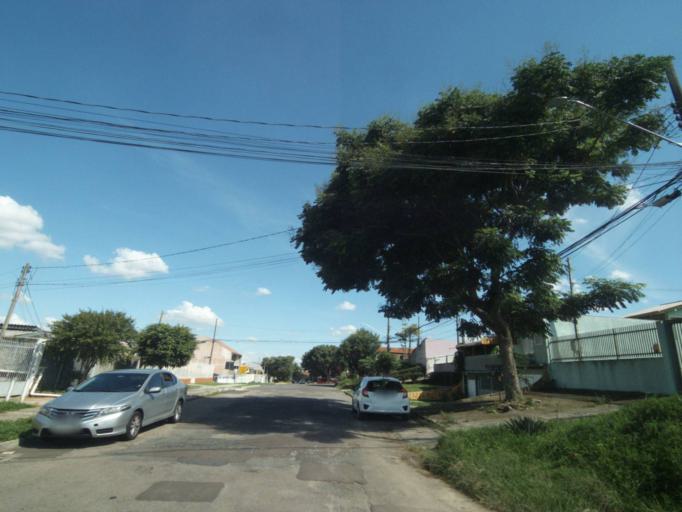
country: BR
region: Parana
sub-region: Pinhais
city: Pinhais
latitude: -25.4619
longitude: -49.2125
